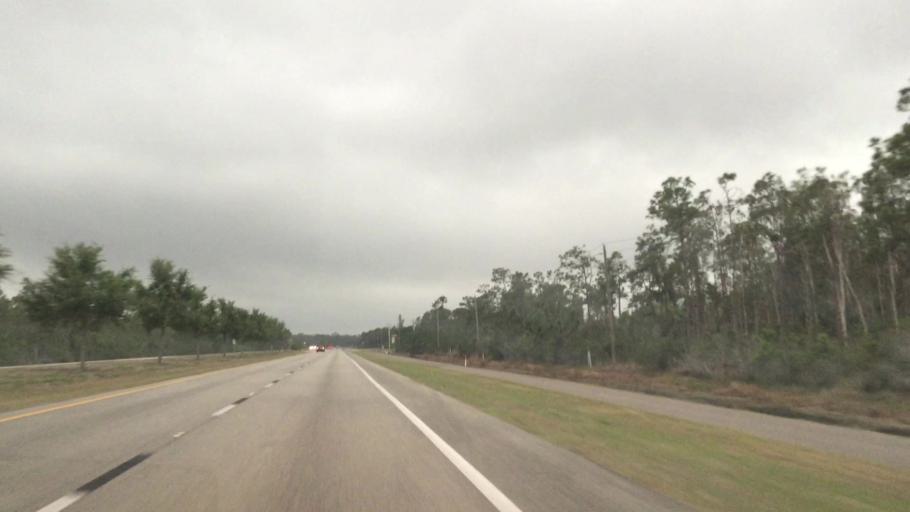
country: US
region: Florida
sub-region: Lee County
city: Villas
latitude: 26.5684
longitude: -81.8289
